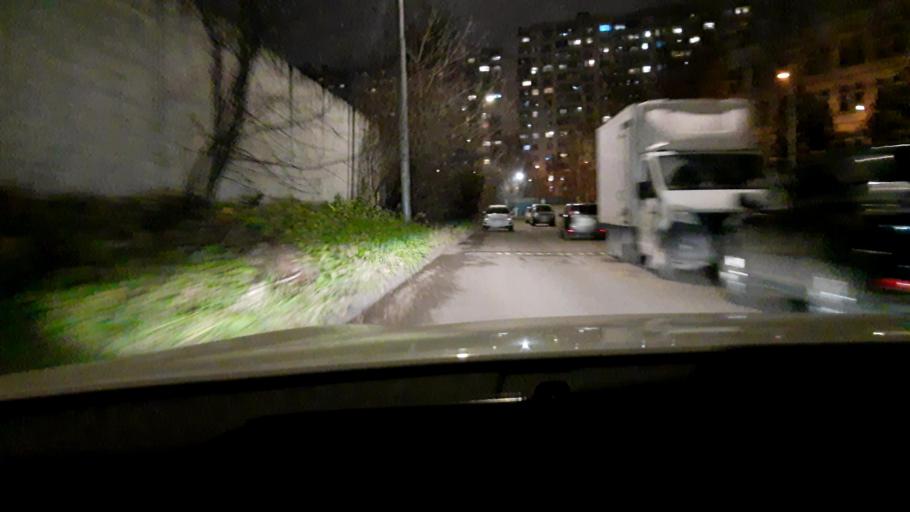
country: RU
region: Moskovskaya
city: Pavshino
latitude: 55.8421
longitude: 37.3483
